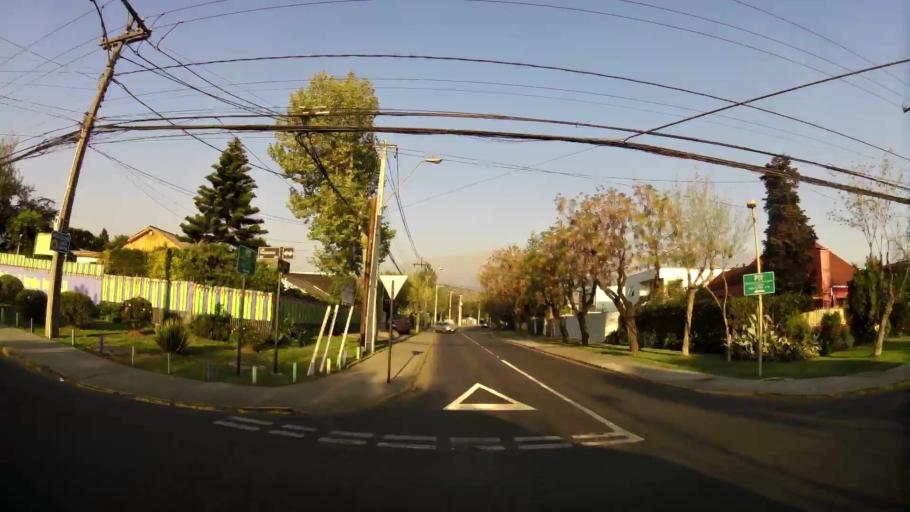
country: CL
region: Santiago Metropolitan
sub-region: Provincia de Santiago
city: Villa Presidente Frei, Nunoa, Santiago, Chile
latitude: -33.3972
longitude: -70.5544
